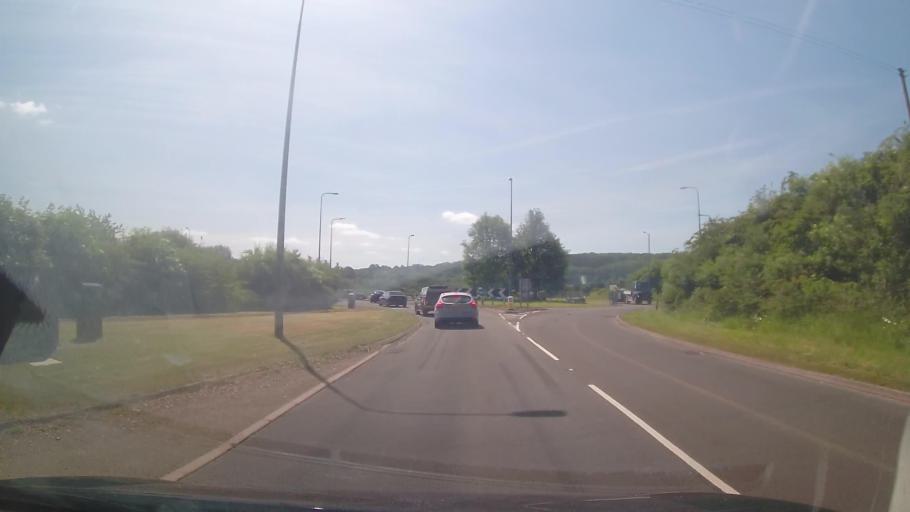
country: GB
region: England
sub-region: Herefordshire
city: Hope under Dinmore
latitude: 52.1795
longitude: -2.7147
